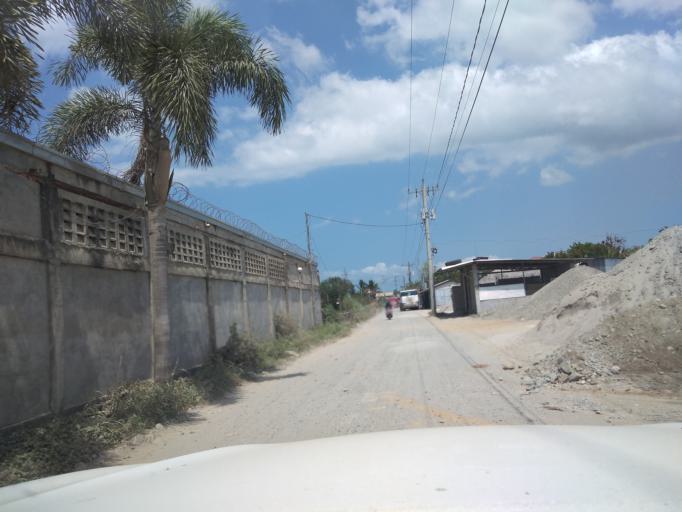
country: PH
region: Central Luzon
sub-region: Province of Pampanga
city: Lourdes
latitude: 15.0174
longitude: 120.8575
